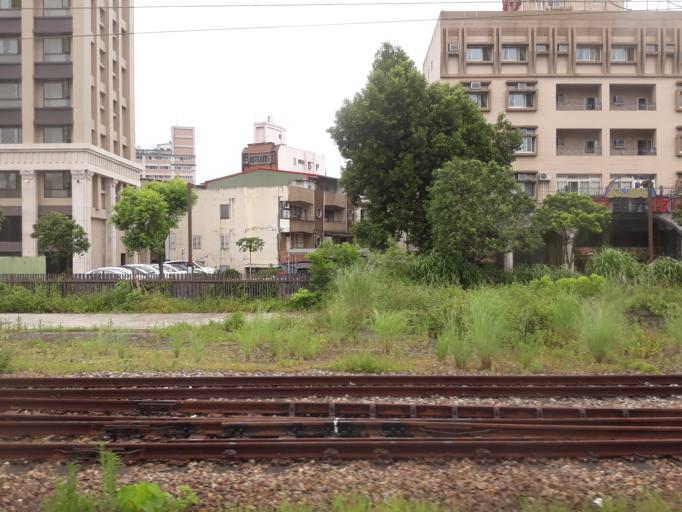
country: TW
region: Taiwan
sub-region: Yilan
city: Yilan
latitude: 24.6797
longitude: 121.7745
